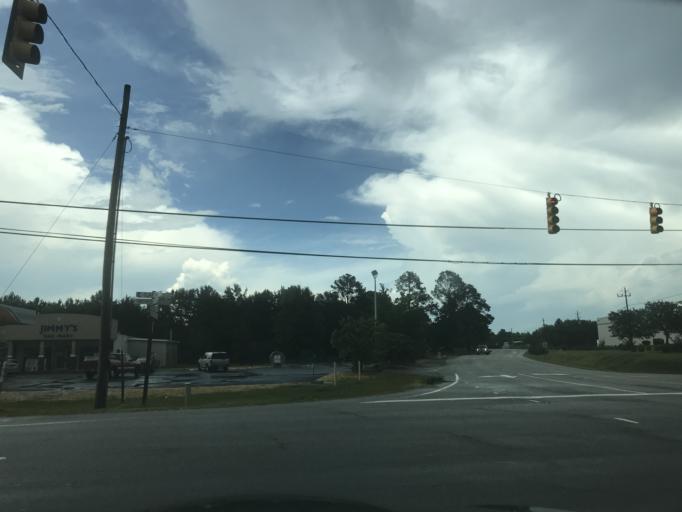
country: US
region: North Carolina
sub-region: Johnston County
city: Wilsons Mills
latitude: 35.5553
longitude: -78.3865
